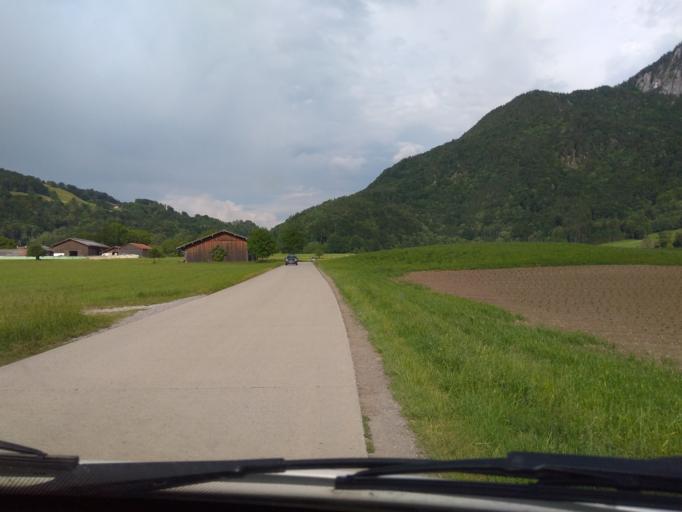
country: DE
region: Bavaria
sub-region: Upper Bavaria
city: Nussdorf am Inn
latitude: 47.7364
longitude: 12.1536
